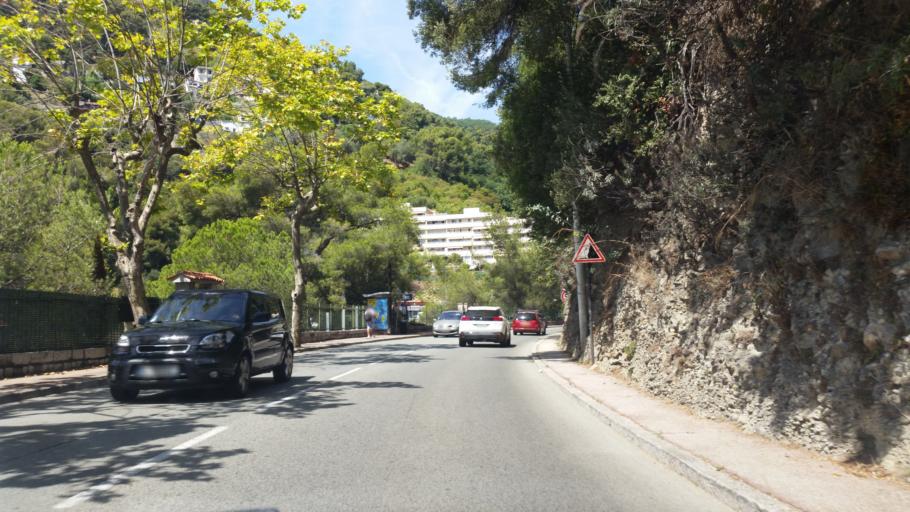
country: MC
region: Commune de Monaco
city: Saint-Roman
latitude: 43.7620
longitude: 7.4555
